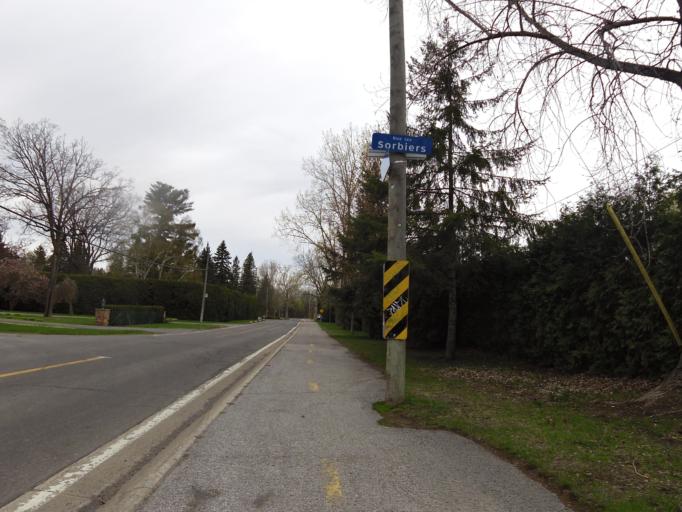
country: CA
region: Quebec
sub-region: Laurentides
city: Deux-Montagnes
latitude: 45.5292
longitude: -73.8790
